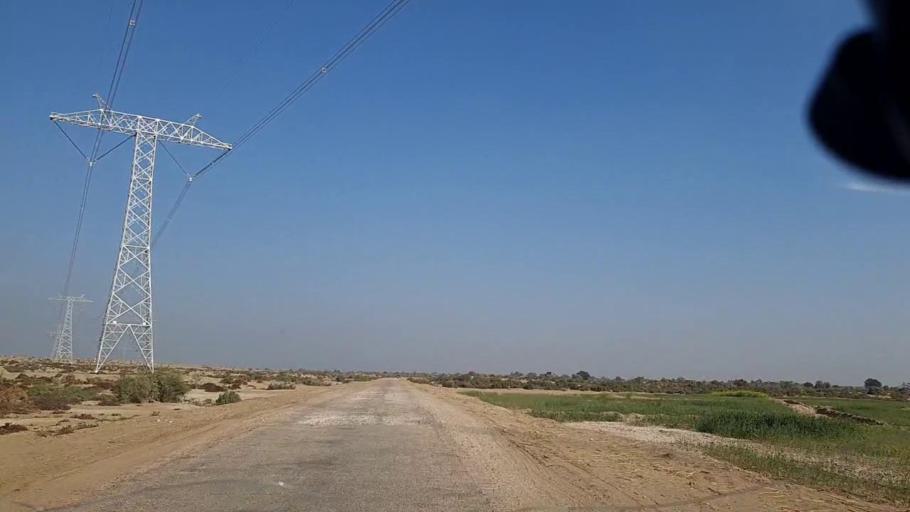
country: PK
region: Sindh
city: Khanpur
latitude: 27.6857
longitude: 69.4663
